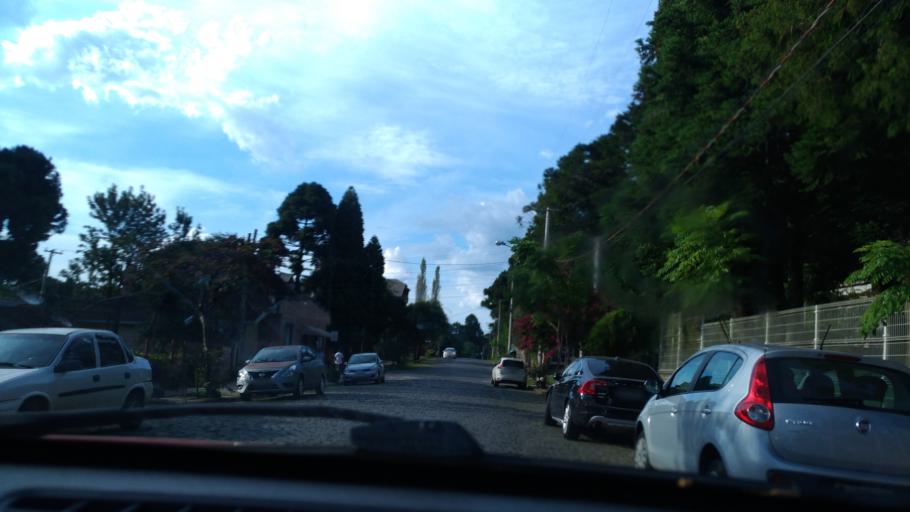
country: BR
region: Rio Grande do Sul
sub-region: Canela
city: Canela
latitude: -29.3570
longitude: -50.8130
